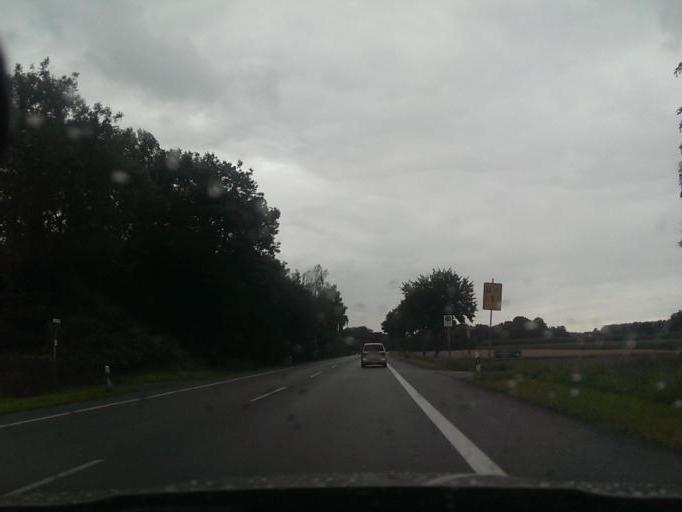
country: DE
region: North Rhine-Westphalia
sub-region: Regierungsbezirk Detmold
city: Delbruck
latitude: 51.7633
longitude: 8.5924
